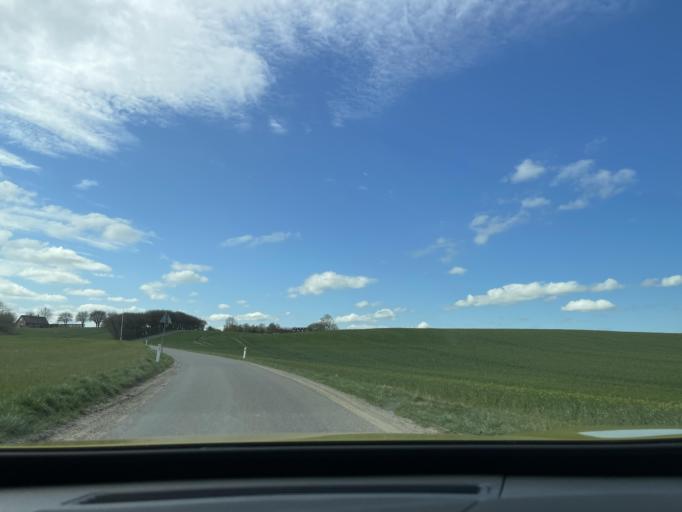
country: DK
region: Central Jutland
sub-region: Favrskov Kommune
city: Hinnerup
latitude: 56.2868
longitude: 10.0837
